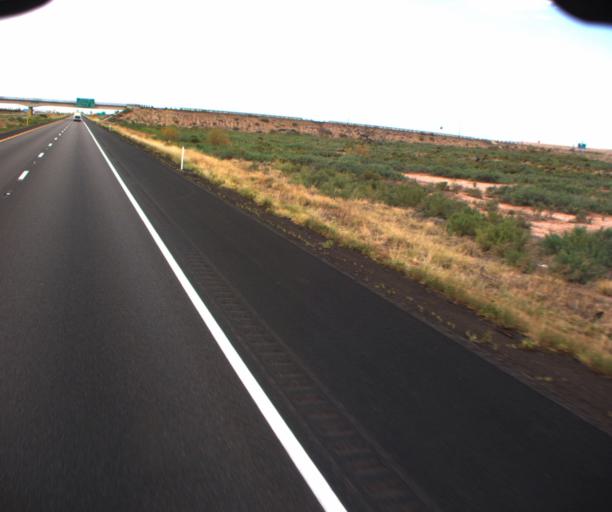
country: US
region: Arizona
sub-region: Navajo County
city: Winslow
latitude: 35.0082
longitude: -110.6387
